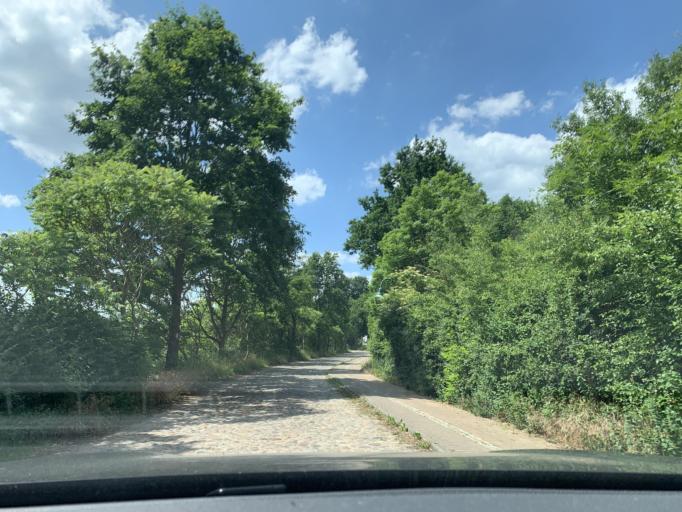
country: DE
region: Brandenburg
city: Rheinsberg
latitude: 53.1542
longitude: 12.7714
